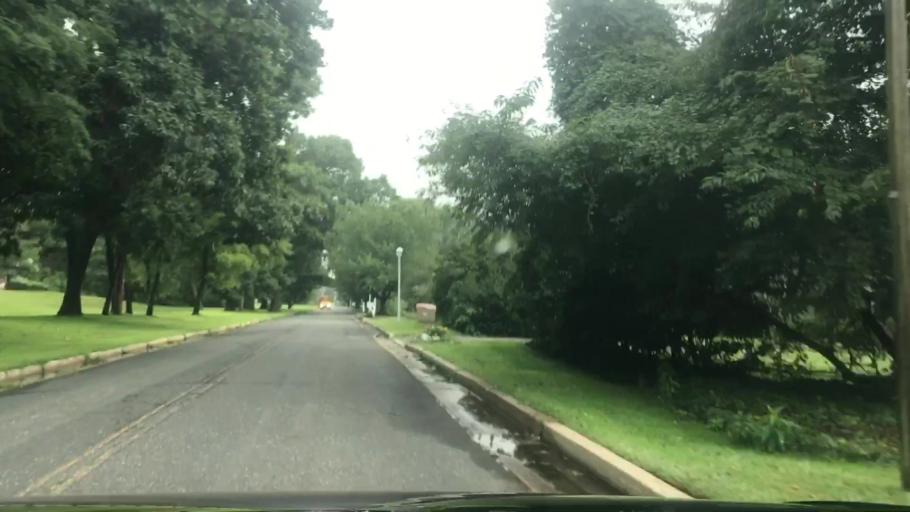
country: US
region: New Jersey
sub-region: Monmouth County
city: Fair Haven
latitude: 40.3488
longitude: -74.0414
